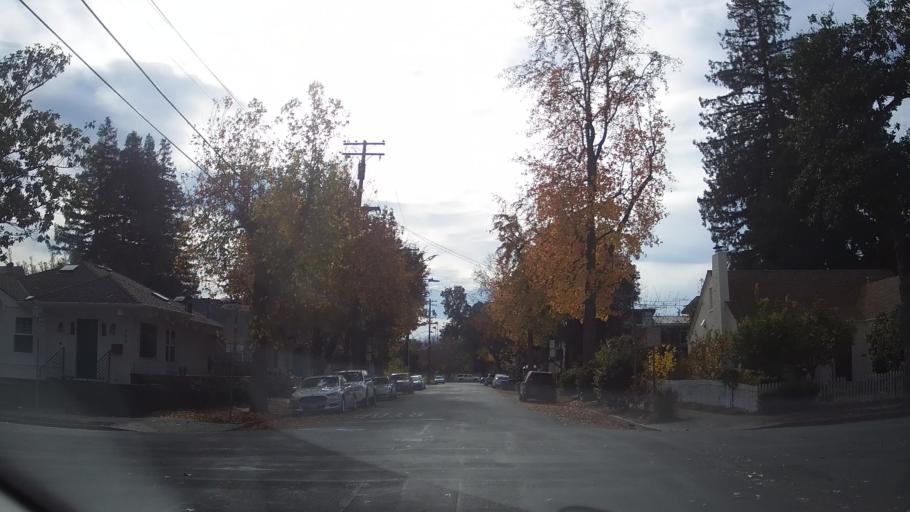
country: US
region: California
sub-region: San Mateo County
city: Menlo Park
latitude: 37.4472
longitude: -122.1665
